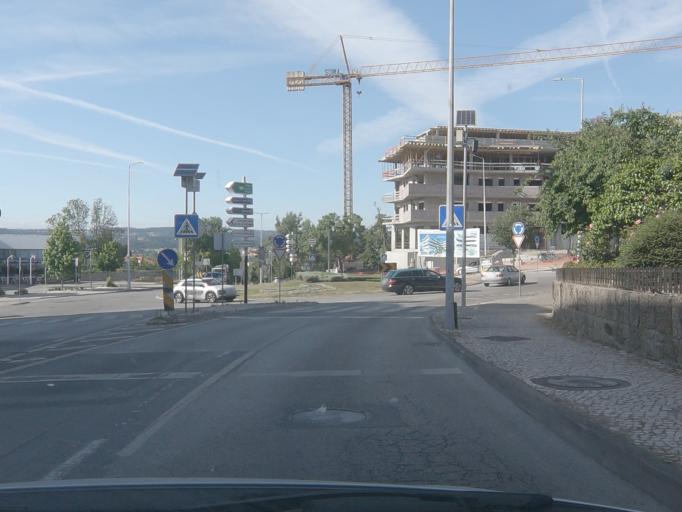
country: PT
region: Viseu
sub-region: Viseu
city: Viseu
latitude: 40.6560
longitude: -7.9063
